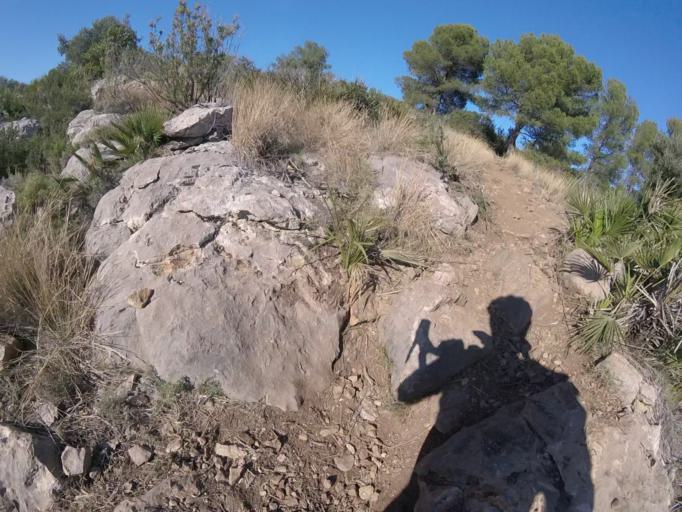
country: ES
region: Valencia
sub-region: Provincia de Castello
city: Orpesa/Oropesa del Mar
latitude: 40.1139
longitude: 0.1166
